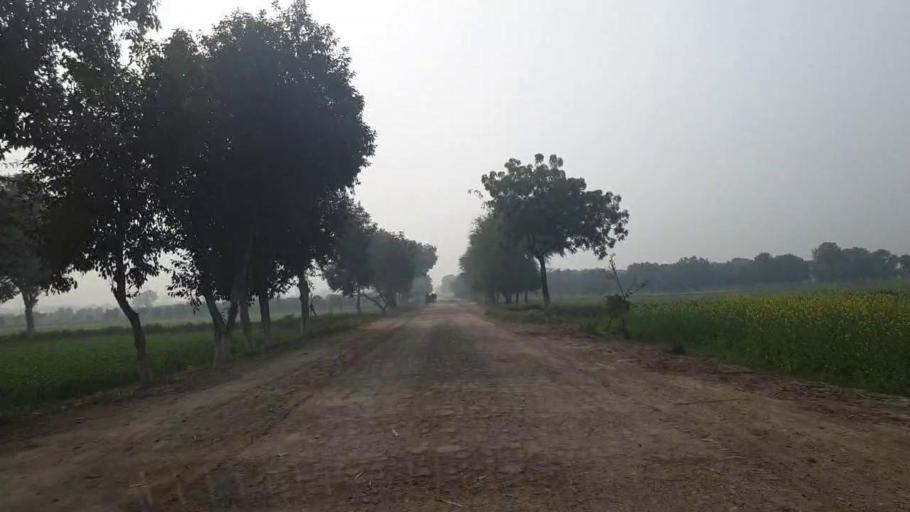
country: PK
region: Sindh
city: Tando Adam
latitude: 25.7880
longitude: 68.6073
